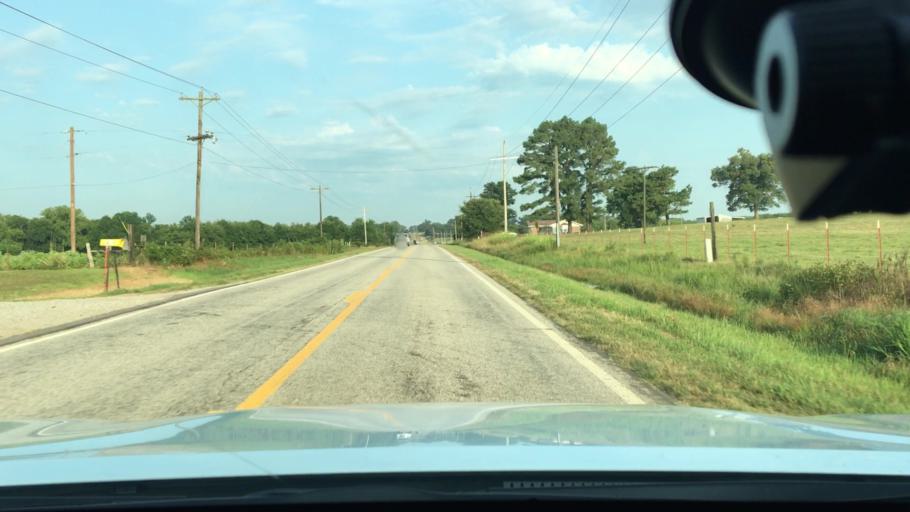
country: US
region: Arkansas
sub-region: Johnson County
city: Coal Hill
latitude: 35.3374
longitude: -93.6211
